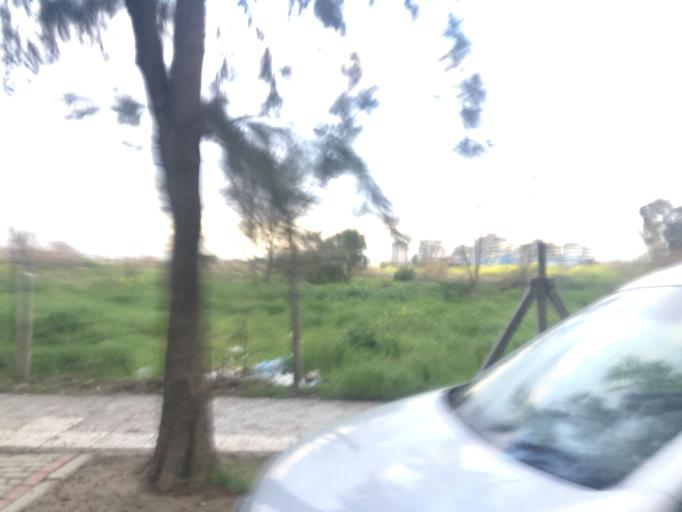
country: TR
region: Izmir
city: Karsiyaka
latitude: 38.4711
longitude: 27.0674
